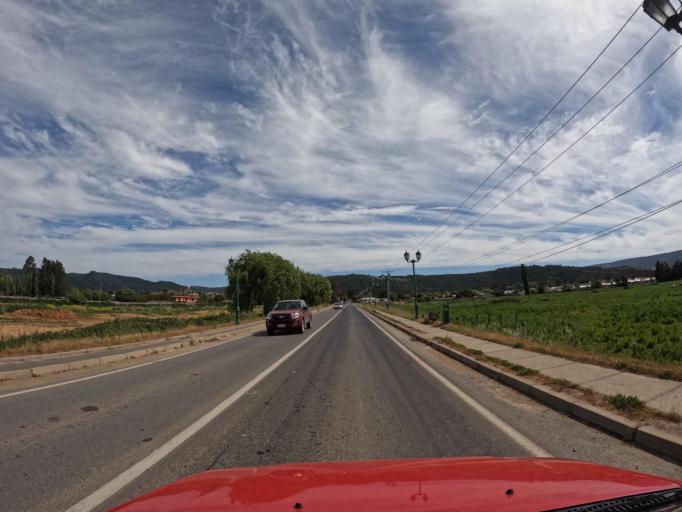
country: CL
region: Maule
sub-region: Provincia de Talca
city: Constitucion
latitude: -35.0870
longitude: -72.0193
